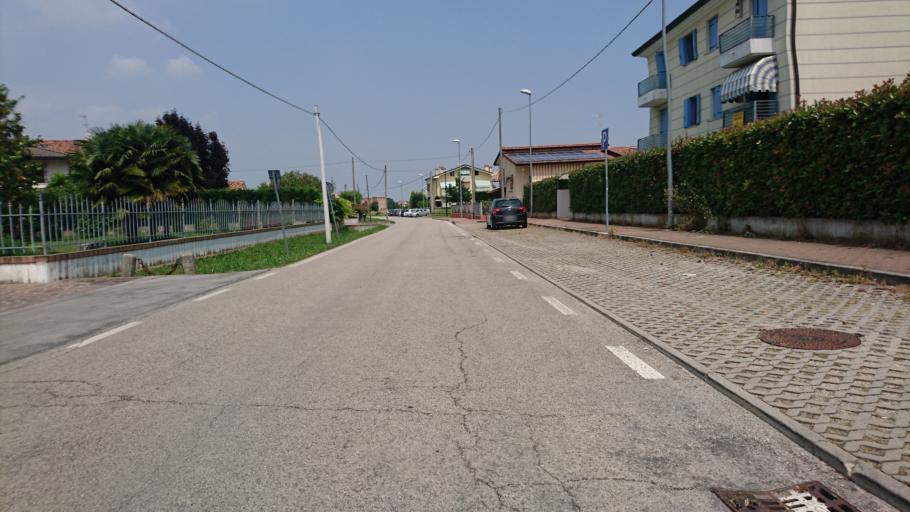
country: IT
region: Veneto
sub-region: Provincia di Padova
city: Cartura
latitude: 45.2700
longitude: 11.8567
